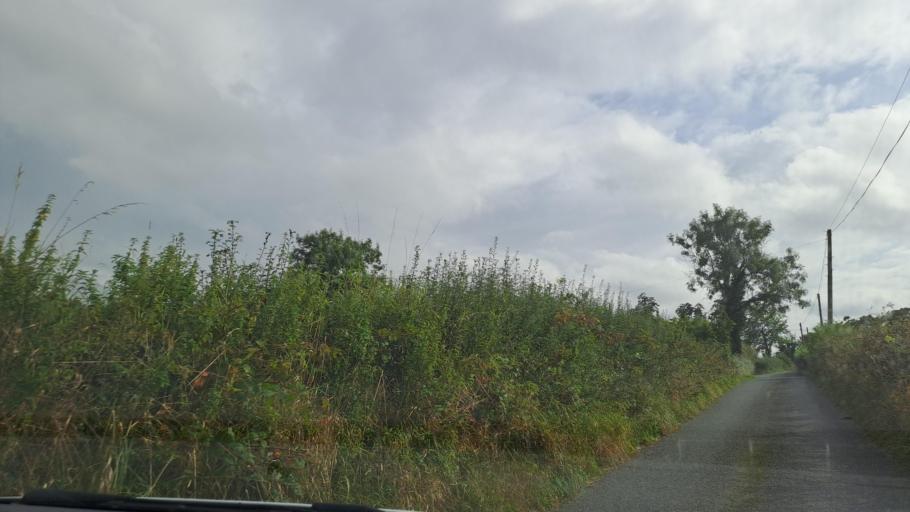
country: IE
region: Ulster
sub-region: An Cabhan
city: Kingscourt
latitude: 53.9845
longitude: -6.8611
